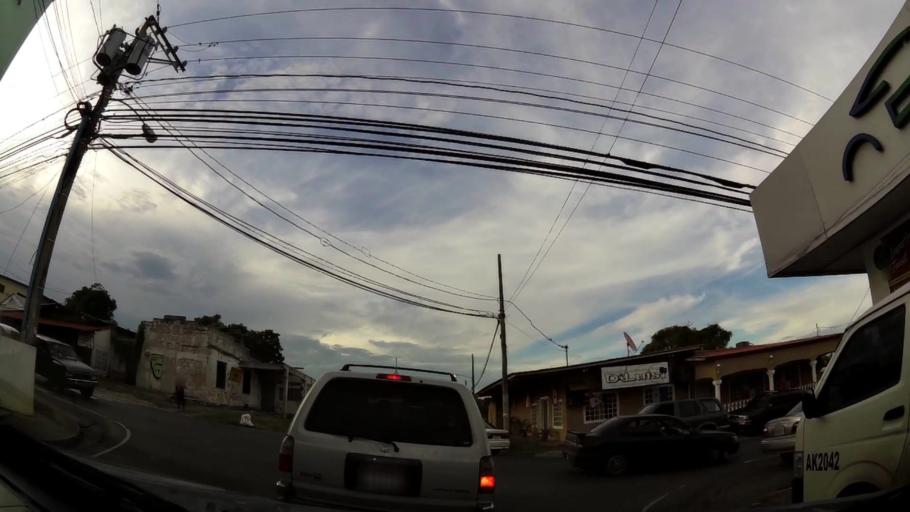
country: PA
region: Panama
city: La Chorrera
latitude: 8.8780
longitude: -79.7854
